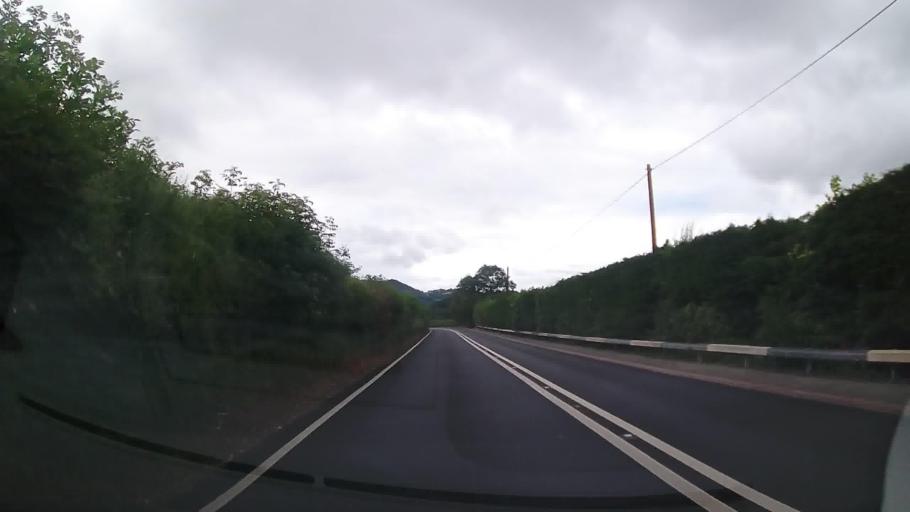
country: GB
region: Wales
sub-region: Denbighshire
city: Llangollen
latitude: 52.9684
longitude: -3.1379
